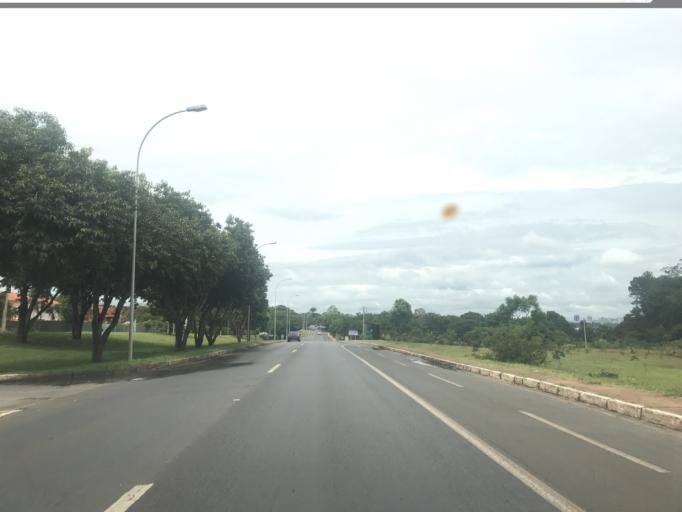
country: BR
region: Federal District
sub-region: Brasilia
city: Brasilia
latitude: -15.8345
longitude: -47.8275
